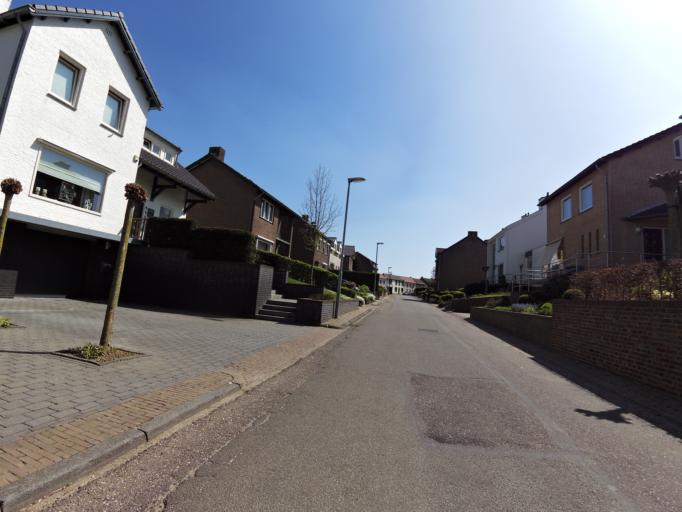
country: NL
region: Limburg
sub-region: Gemeente Voerendaal
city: Ubachsberg
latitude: 50.8545
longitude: 5.9514
